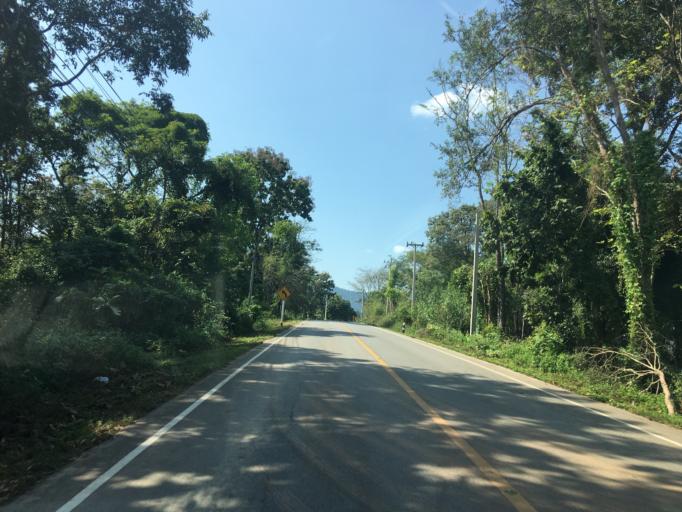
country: TH
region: Nan
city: Ban Luang
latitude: 18.8449
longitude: 100.4045
